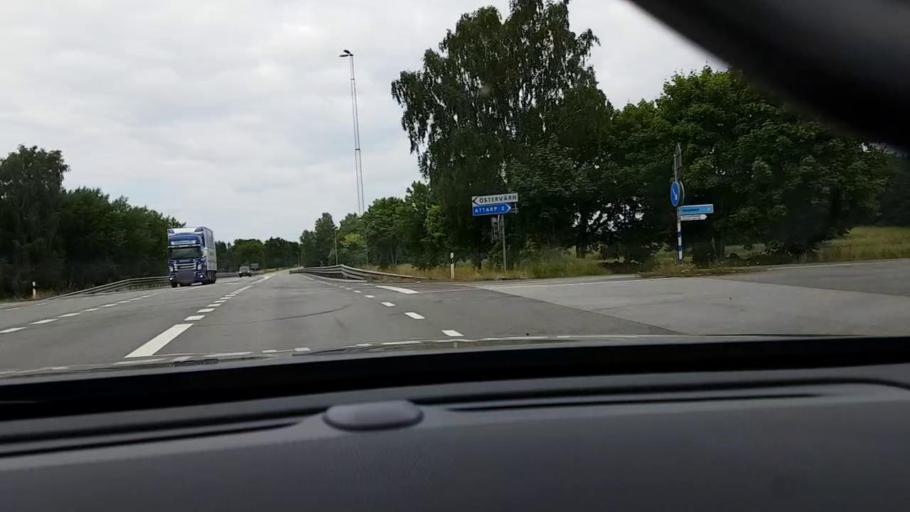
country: SE
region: Skane
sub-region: Hassleholms Kommun
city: Hassleholm
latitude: 56.1484
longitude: 13.8061
